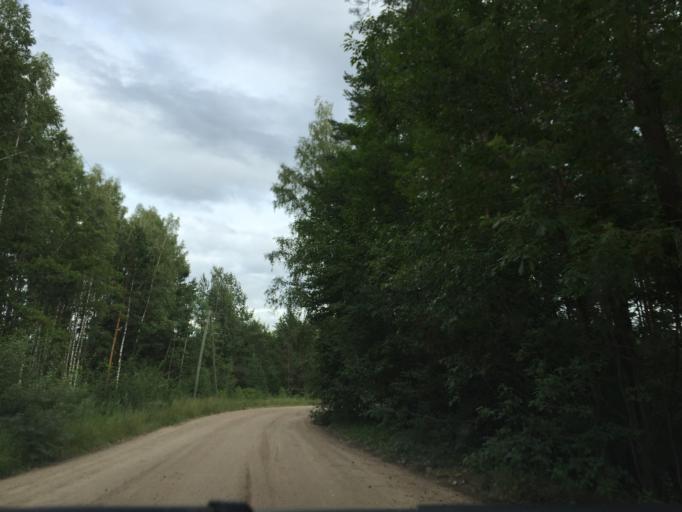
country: LV
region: Saulkrastu
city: Saulkrasti
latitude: 57.1908
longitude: 24.3623
